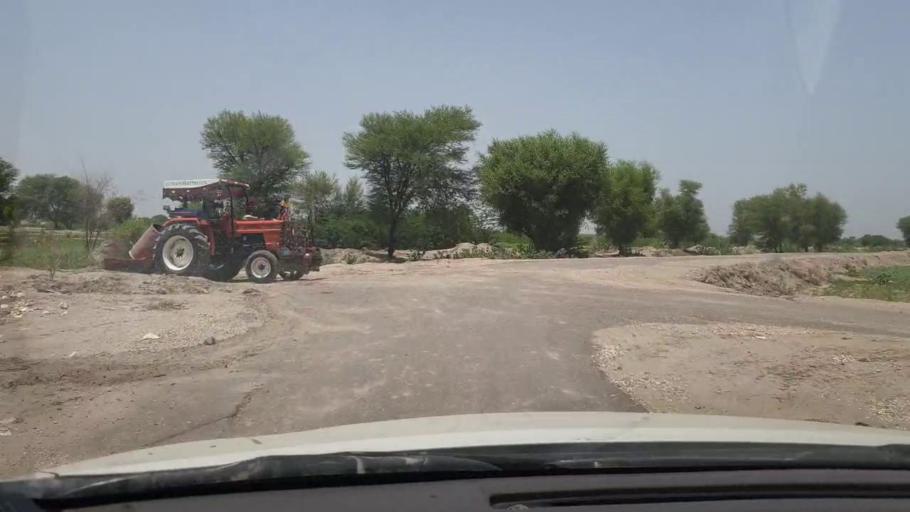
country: PK
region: Sindh
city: Rohri
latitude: 27.5177
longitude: 69.1787
